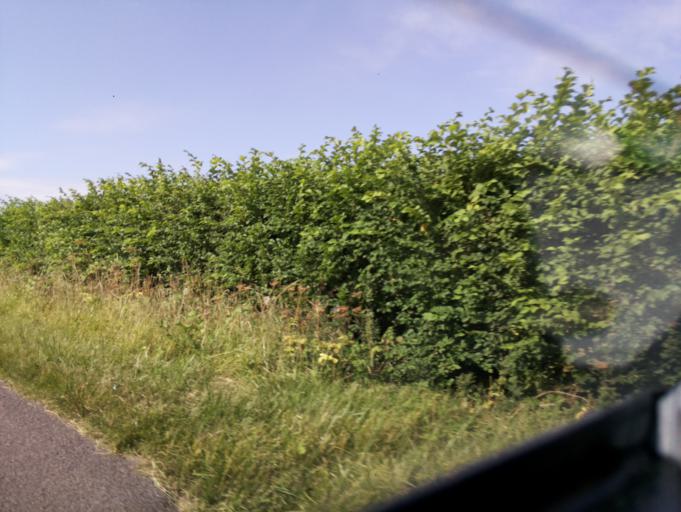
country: GB
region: England
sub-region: Oxfordshire
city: Faringdon
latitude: 51.6768
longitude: -1.5887
